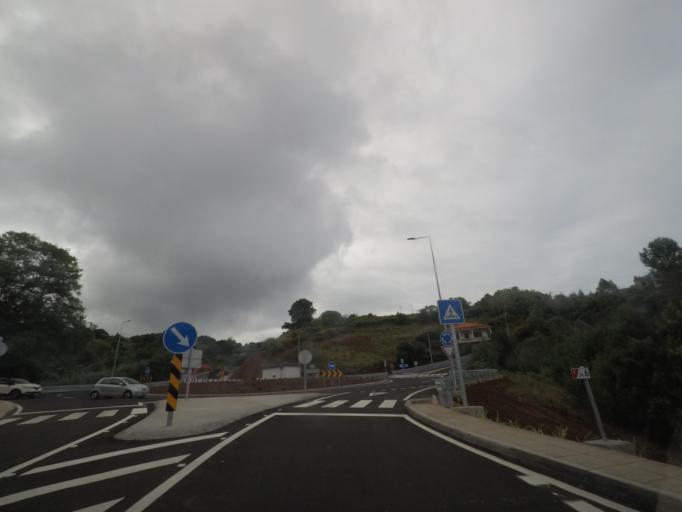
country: PT
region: Madeira
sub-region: Santana
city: Santana
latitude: 32.8303
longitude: -16.9075
